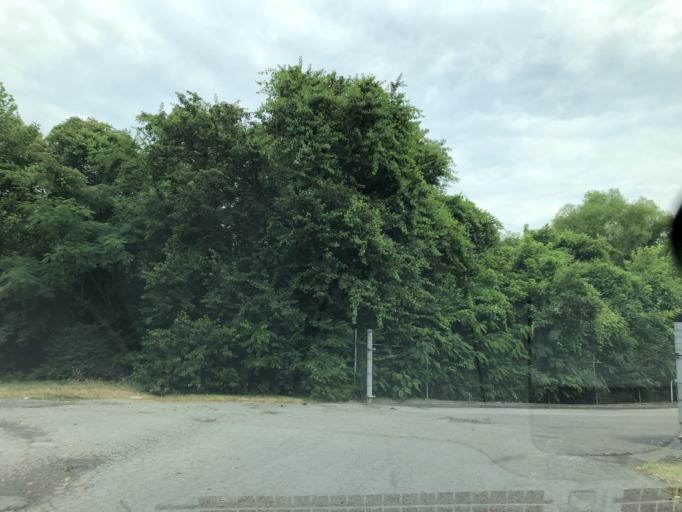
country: US
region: Tennessee
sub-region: Davidson County
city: Oak Hill
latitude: 36.0713
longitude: -86.6808
